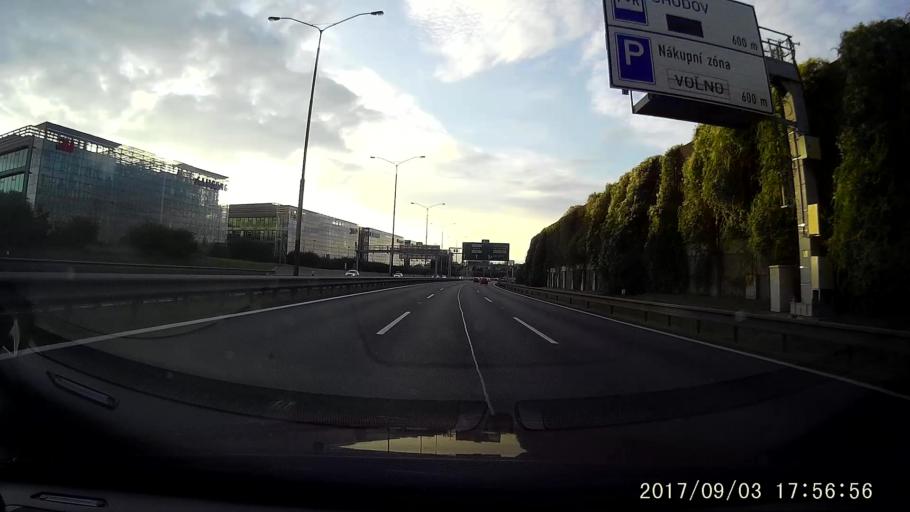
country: CZ
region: Central Bohemia
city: Vestec
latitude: 50.0265
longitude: 14.4989
